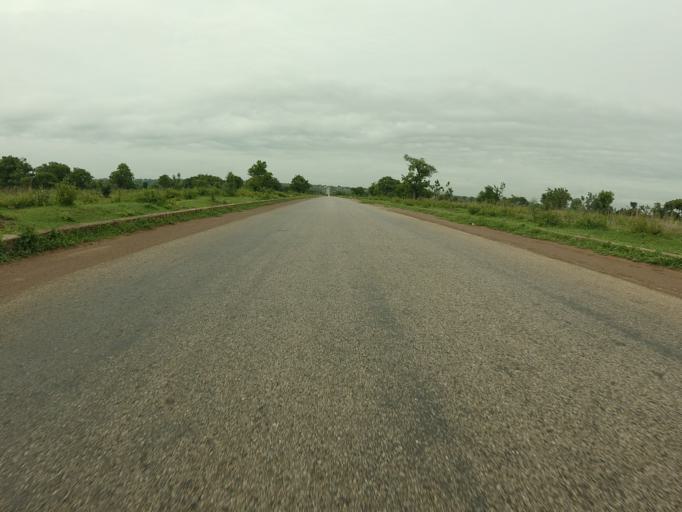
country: GH
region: Northern
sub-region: Yendi
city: Yendi
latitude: 9.5014
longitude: -0.0253
